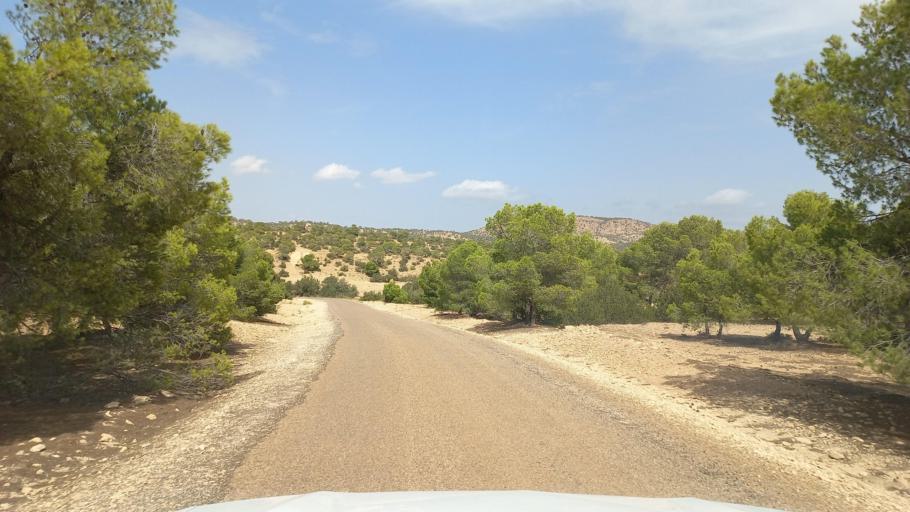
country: TN
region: Al Qasrayn
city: Sbiba
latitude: 35.4088
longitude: 8.9291
